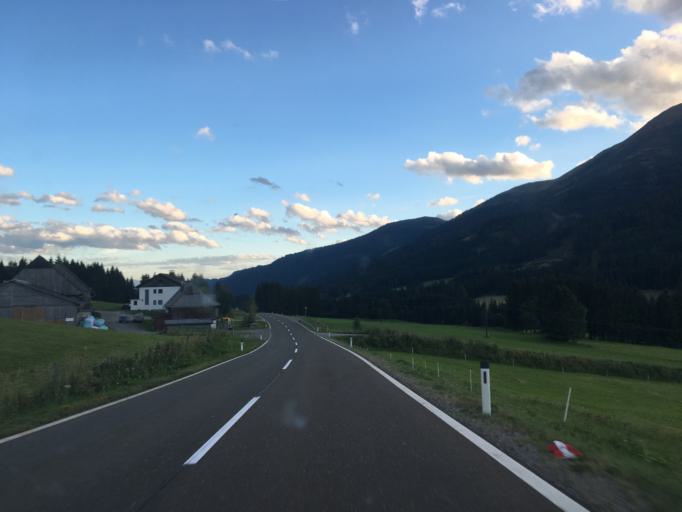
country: AT
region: Styria
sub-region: Politischer Bezirk Murtal
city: Hohentauern
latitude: 47.4048
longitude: 14.4636
